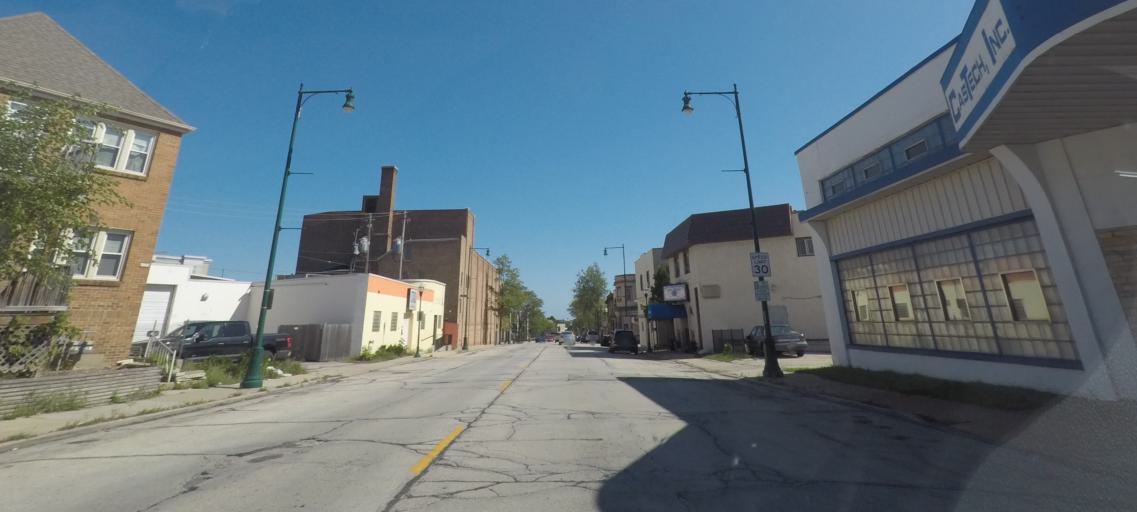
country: US
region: Wisconsin
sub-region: Milwaukee County
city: West Allis
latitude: 43.0159
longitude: -87.9919
